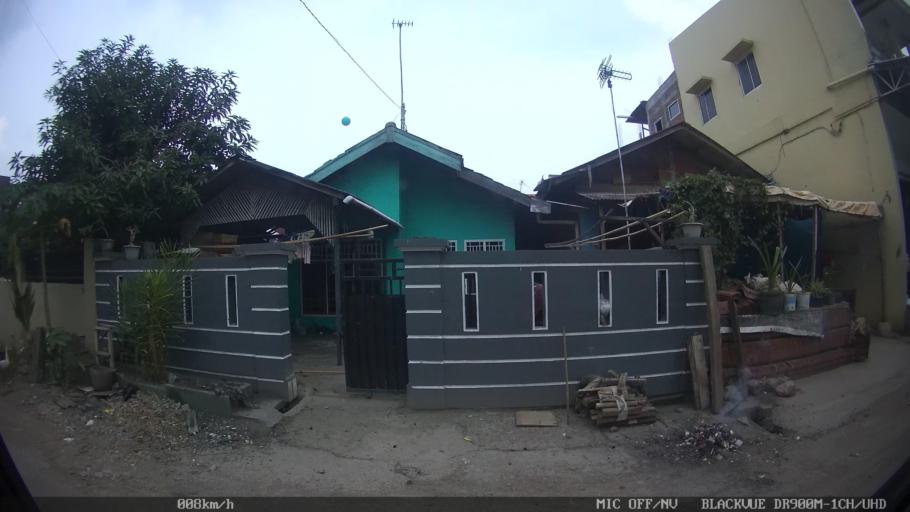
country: ID
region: Lampung
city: Bandarlampung
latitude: -5.4401
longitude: 105.2836
